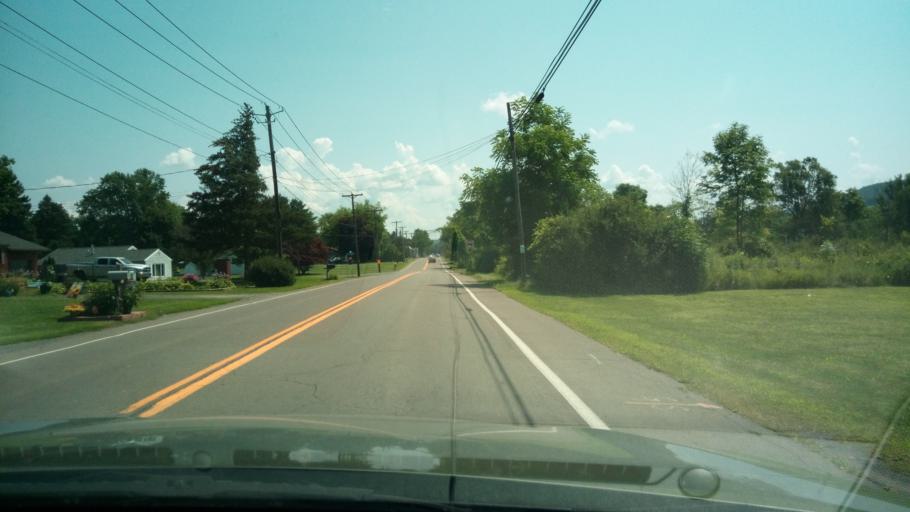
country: US
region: New York
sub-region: Chemung County
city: Horseheads North
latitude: 42.1902
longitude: -76.8193
